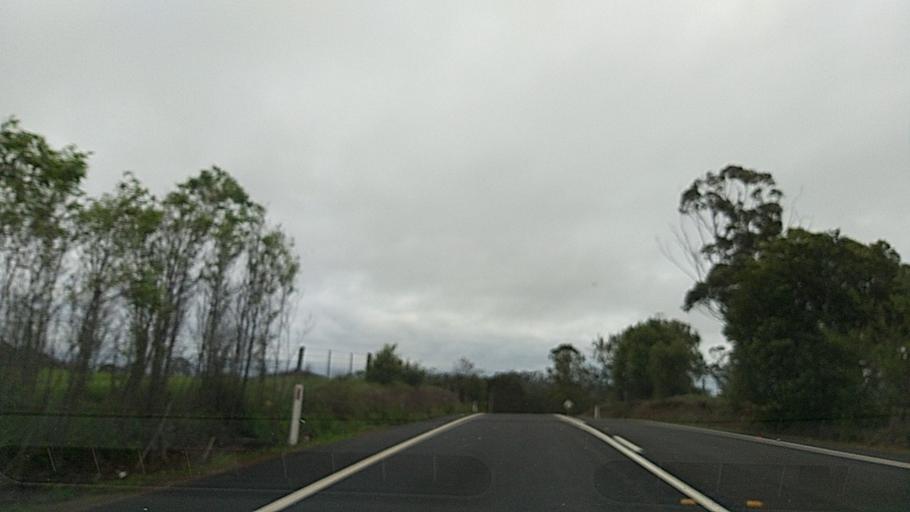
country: AU
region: New South Wales
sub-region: Wollondilly
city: Douglas Park
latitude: -34.1334
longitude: 150.7097
